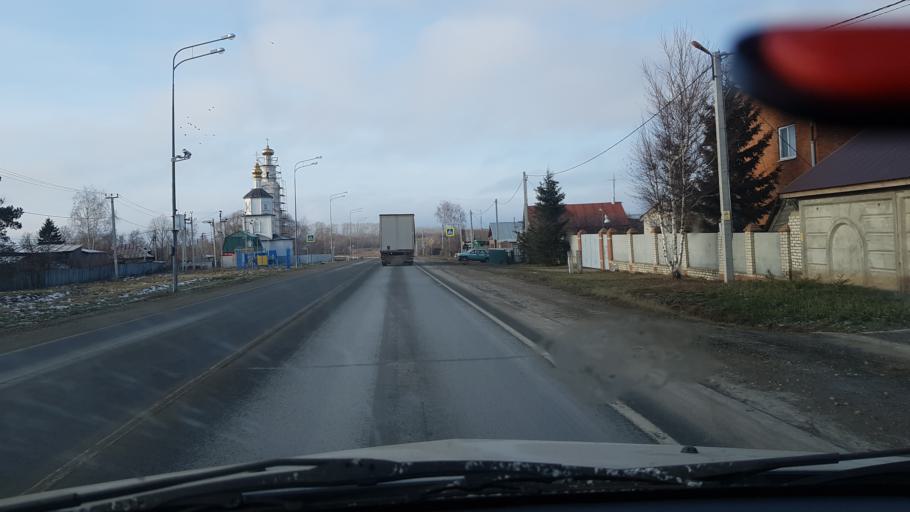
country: RU
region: Tatarstan
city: Laishevo
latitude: 55.3919
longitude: 49.8034
